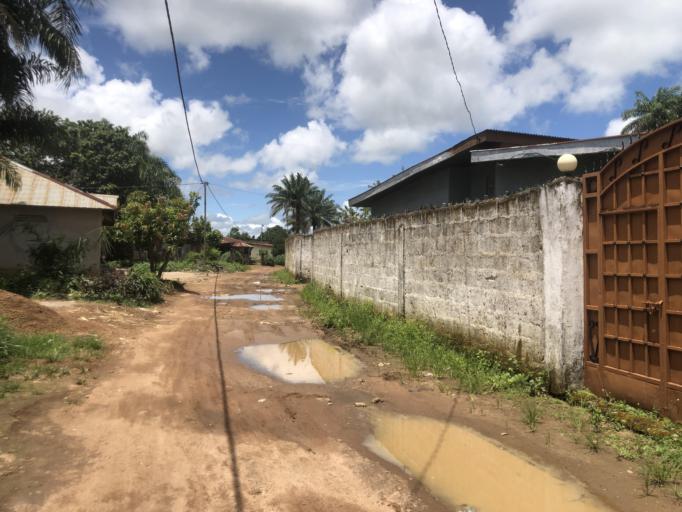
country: SL
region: Northern Province
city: Makeni
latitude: 8.8642
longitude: -12.0528
